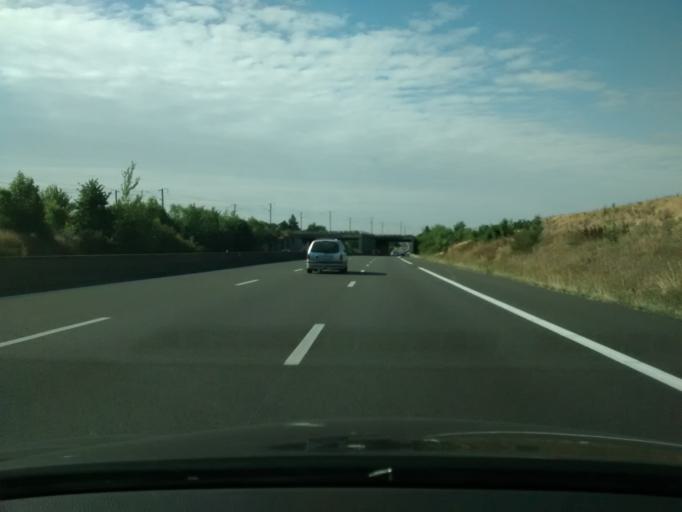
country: FR
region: Ile-de-France
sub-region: Departement de l'Essonne
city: Corbreuse
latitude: 48.5186
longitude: 1.9082
